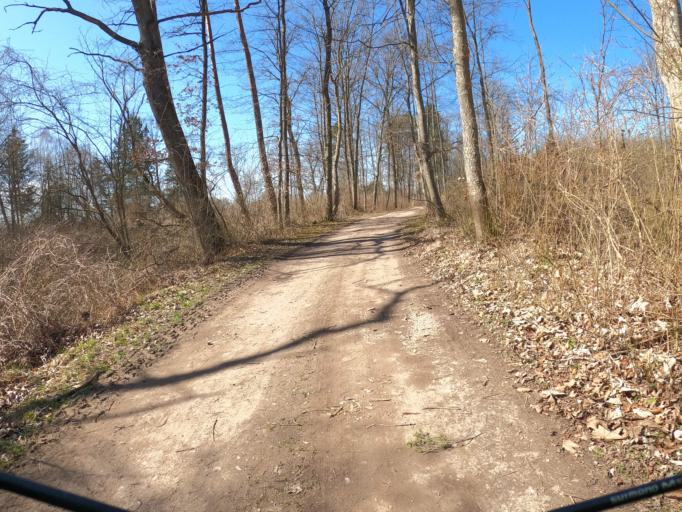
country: DE
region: Bavaria
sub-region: Swabia
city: Nersingen
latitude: 48.4366
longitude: 10.1450
